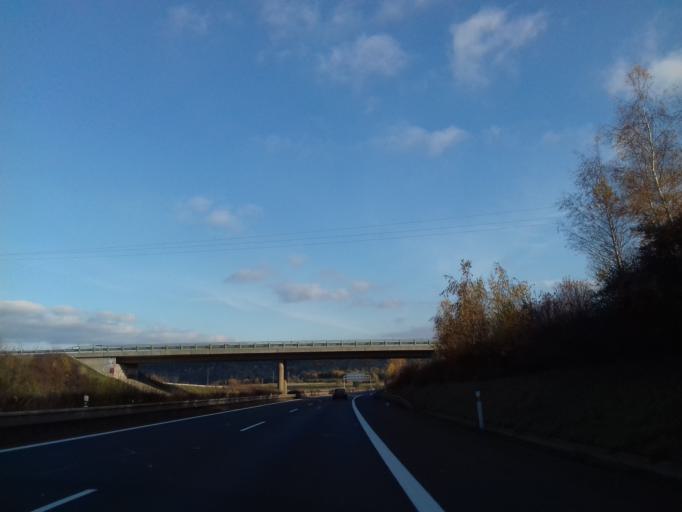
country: CZ
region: Plzensky
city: Stenovice
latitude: 49.6853
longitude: 13.3828
